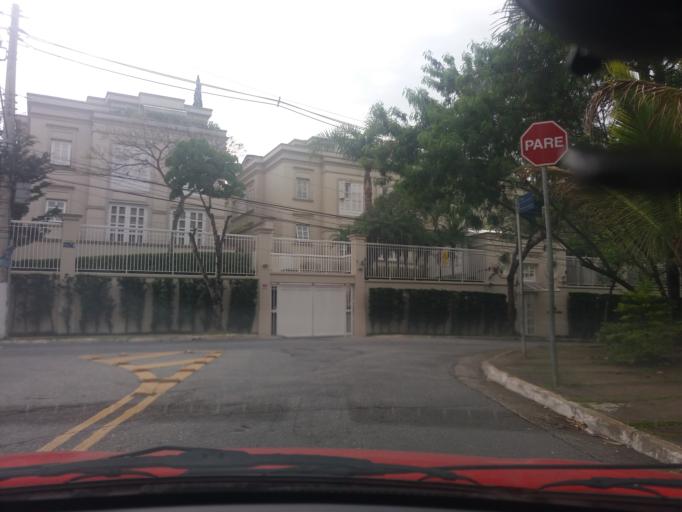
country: BR
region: Sao Paulo
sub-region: Taboao Da Serra
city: Taboao da Serra
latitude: -23.5945
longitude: -46.7144
